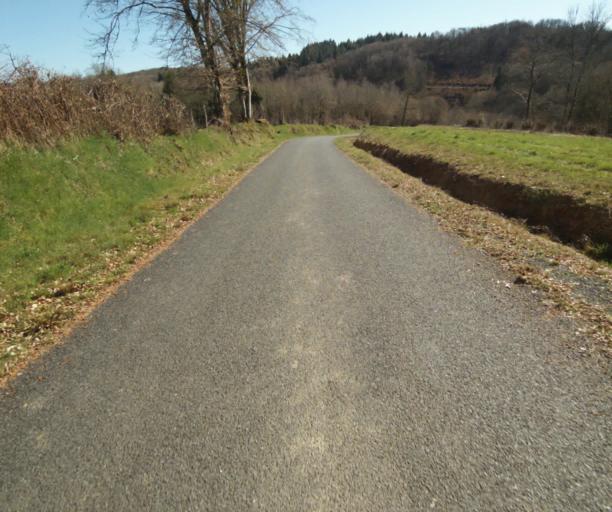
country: FR
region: Limousin
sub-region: Departement de la Correze
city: Chamboulive
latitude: 45.4208
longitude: 1.6476
